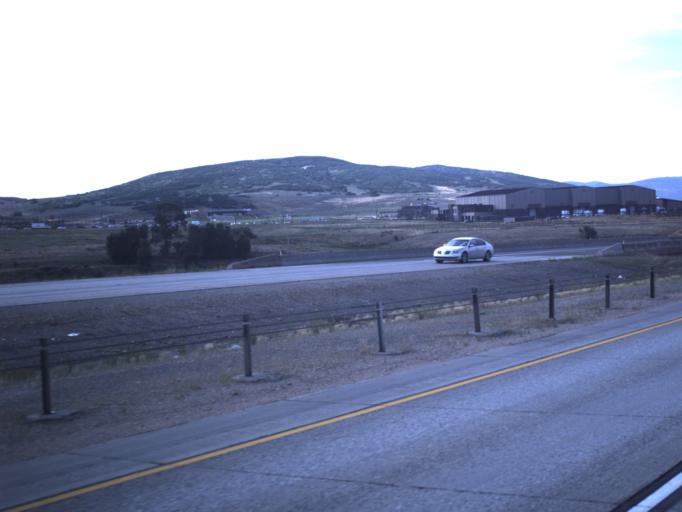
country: US
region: Utah
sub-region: Summit County
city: Park City
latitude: 40.6765
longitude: -111.4607
